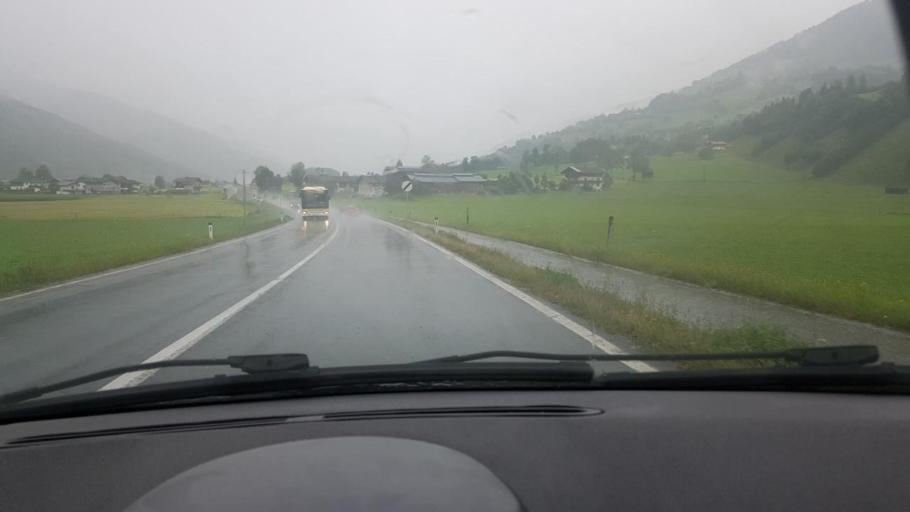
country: AT
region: Salzburg
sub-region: Politischer Bezirk Zell am See
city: Niedernsill
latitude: 47.2842
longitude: 12.6392
